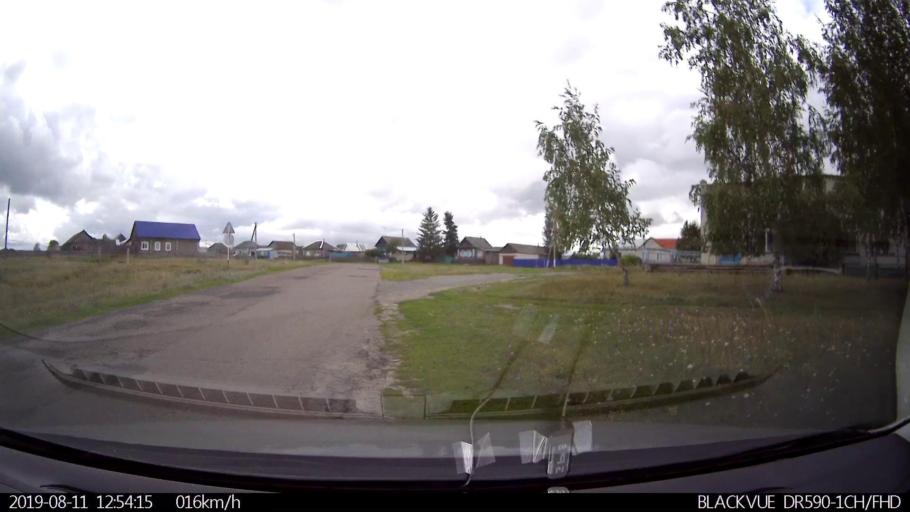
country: RU
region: Ulyanovsk
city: Ignatovka
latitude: 53.8740
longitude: 47.6490
